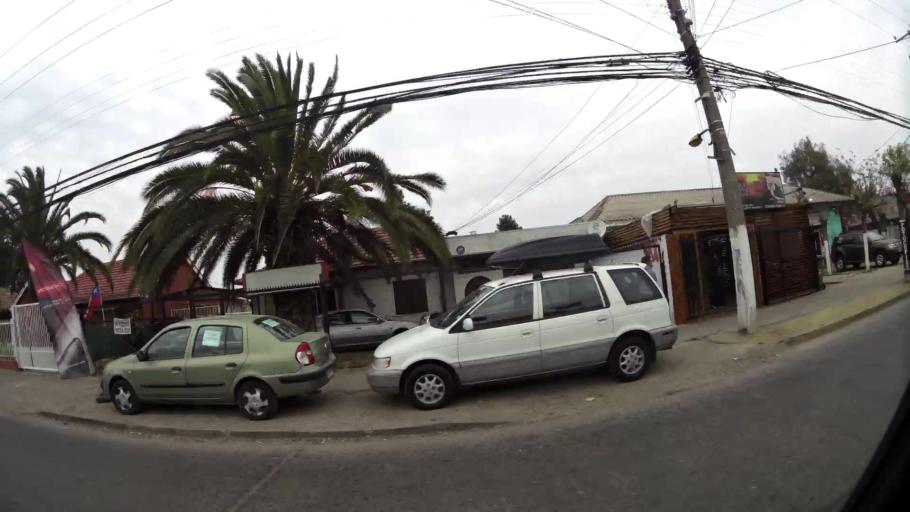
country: CL
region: Santiago Metropolitan
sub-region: Provincia de Santiago
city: Lo Prado
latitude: -33.5003
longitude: -70.7544
